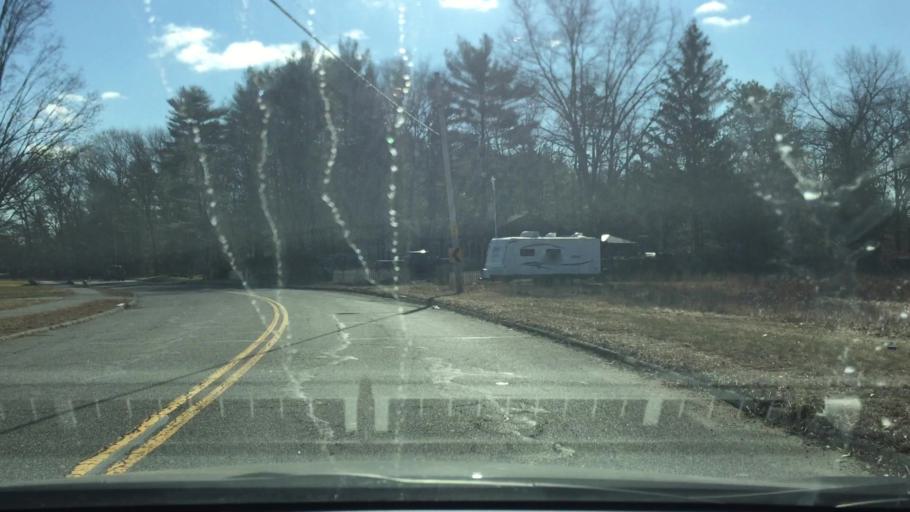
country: US
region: Massachusetts
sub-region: Hampden County
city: Ludlow
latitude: 42.1754
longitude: -72.4928
